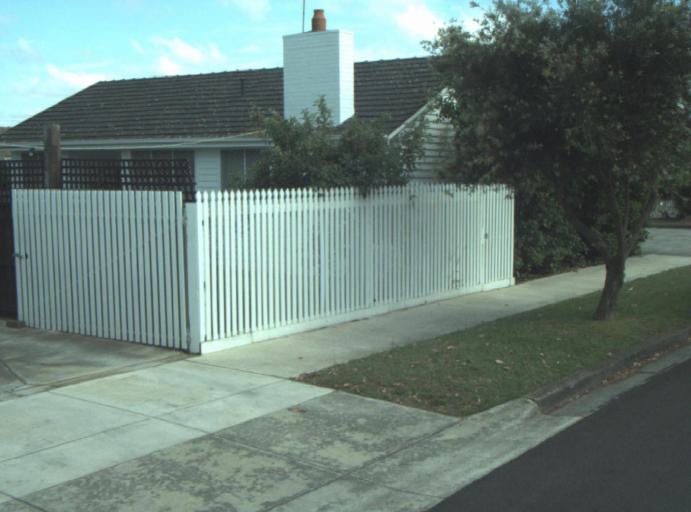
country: AU
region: Victoria
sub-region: Greater Geelong
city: Breakwater
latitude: -38.1705
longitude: 144.3373
